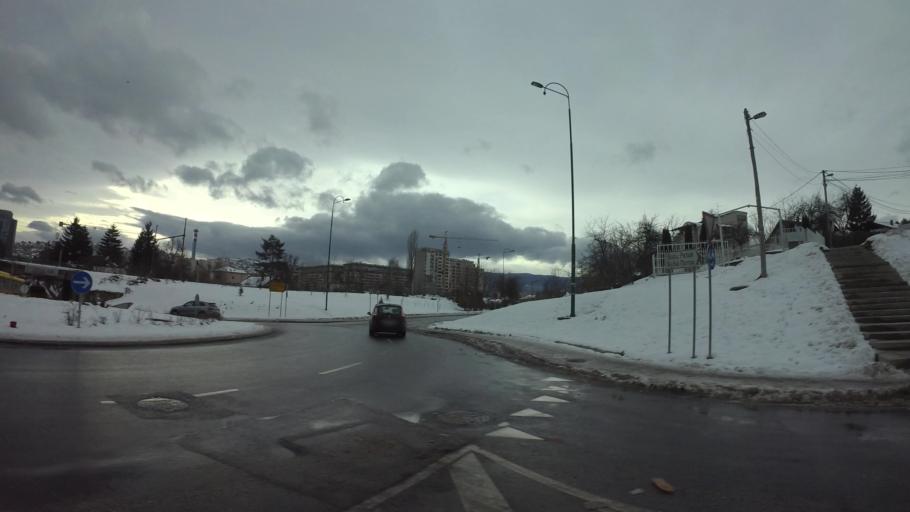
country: BA
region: Federation of Bosnia and Herzegovina
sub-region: Kanton Sarajevo
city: Sarajevo
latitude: 43.8541
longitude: 18.3647
